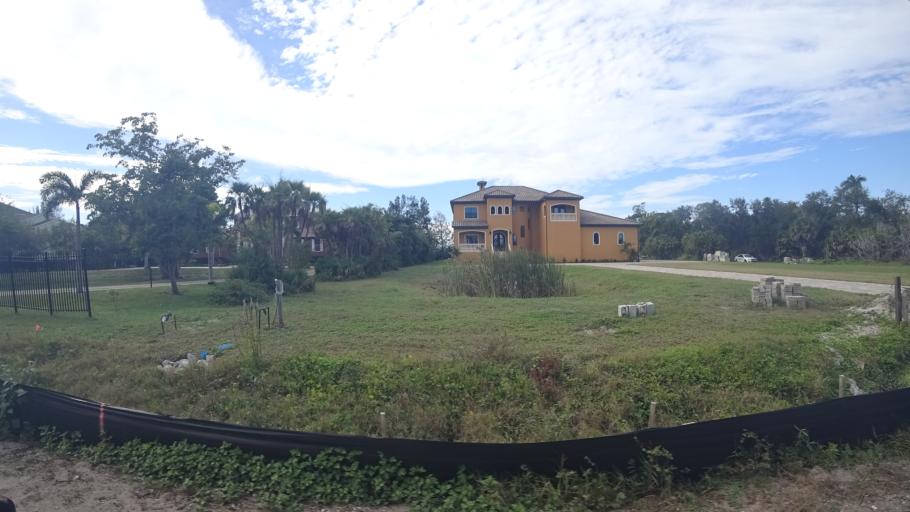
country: US
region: Florida
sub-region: Manatee County
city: West Bradenton
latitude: 27.5097
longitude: -82.6610
